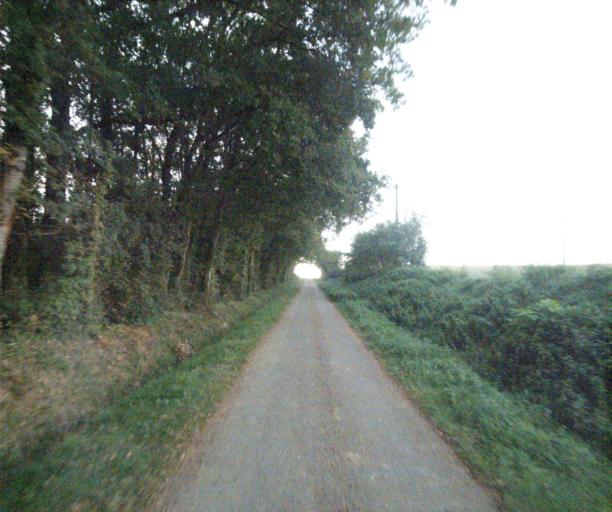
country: FR
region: Midi-Pyrenees
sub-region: Departement du Gers
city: Vic-Fezensac
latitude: 43.7903
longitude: 0.2351
